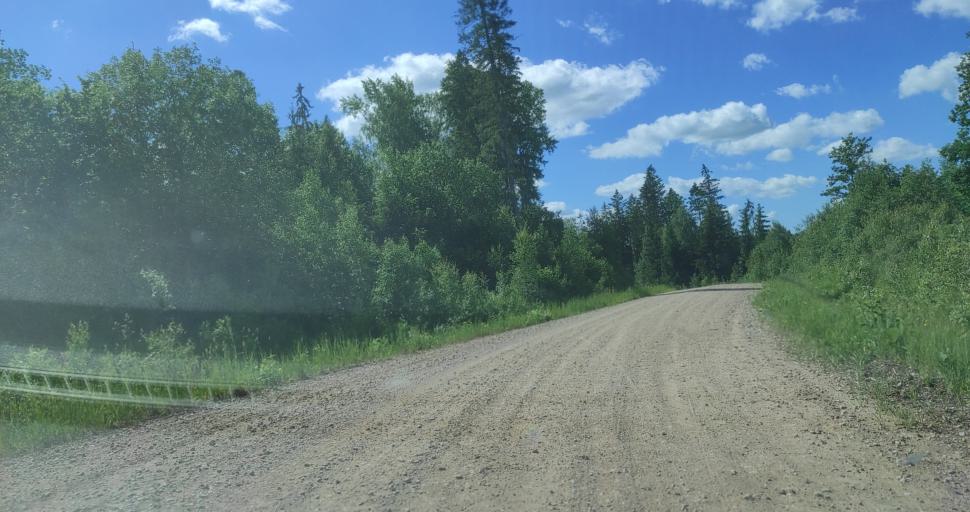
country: LV
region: Kuldigas Rajons
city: Kuldiga
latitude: 56.9314
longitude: 21.7966
